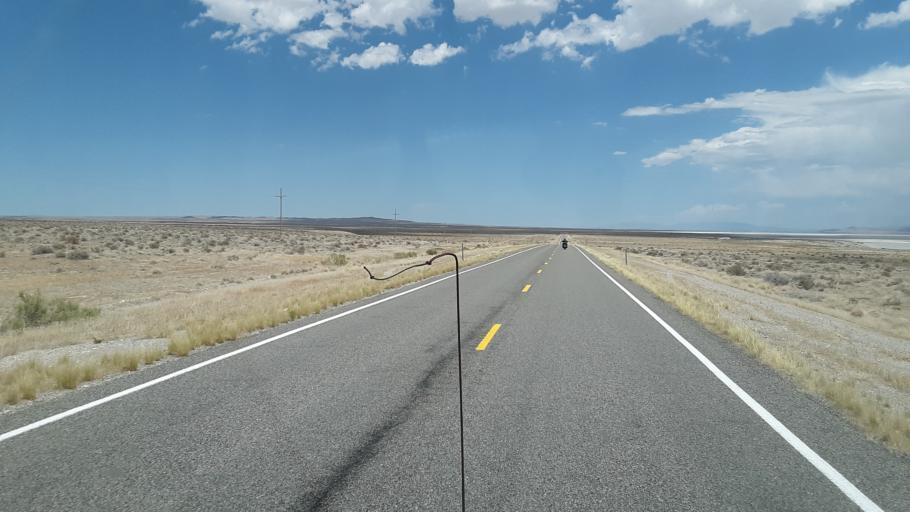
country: US
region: Utah
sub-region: Millard County
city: Delta
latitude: 39.0784
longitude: -113.2032
